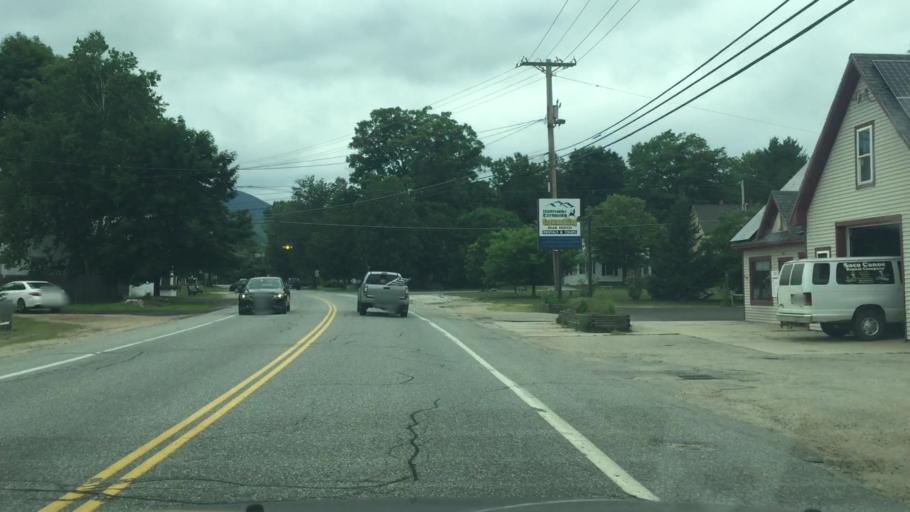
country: US
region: New Hampshire
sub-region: Carroll County
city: North Conway
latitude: 44.0783
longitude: -71.2810
